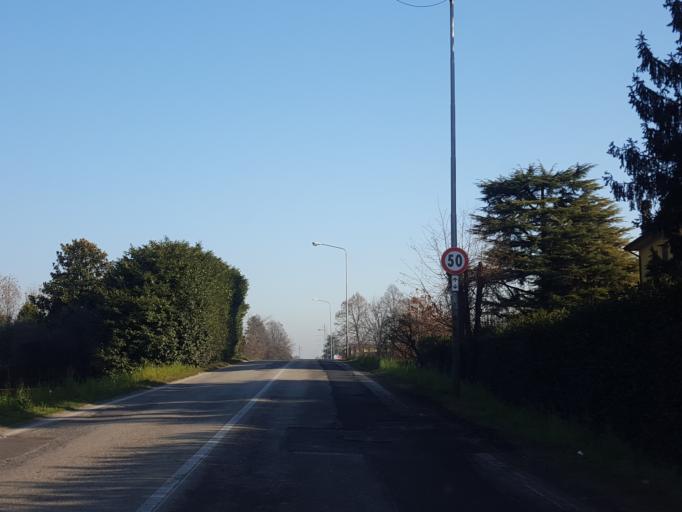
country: IT
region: Veneto
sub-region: Provincia di Vicenza
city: Villaggio Montegrappa
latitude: 45.5432
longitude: 11.6085
